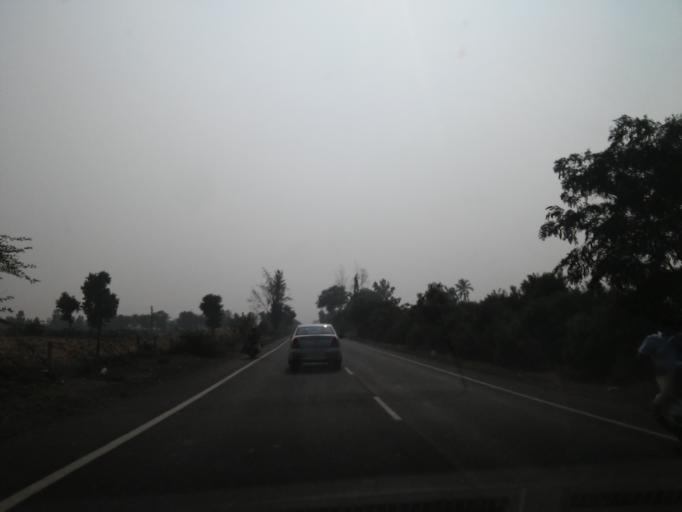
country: IN
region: Gujarat
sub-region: Kachchh
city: Mandvi
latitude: 22.8712
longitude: 69.3938
